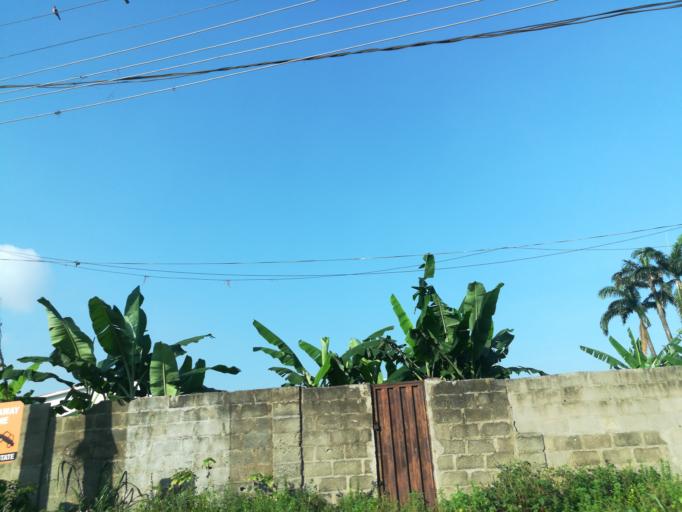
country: NG
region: Lagos
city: Ojota
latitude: 6.5846
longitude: 3.3667
